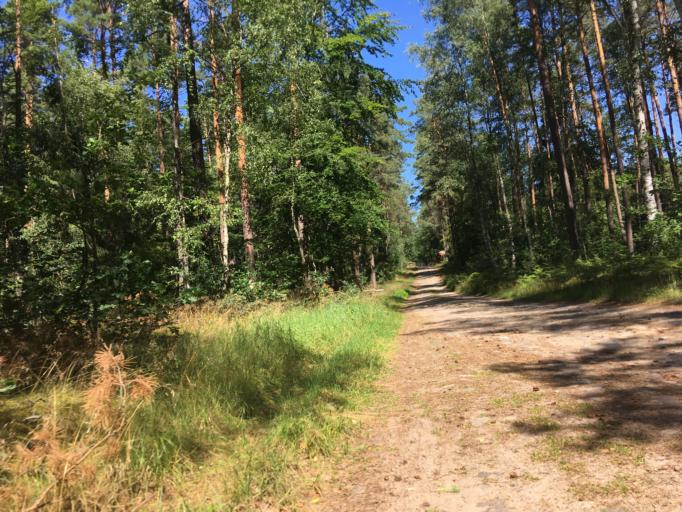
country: DE
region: Brandenburg
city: Rheinsberg
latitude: 53.1093
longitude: 12.9567
